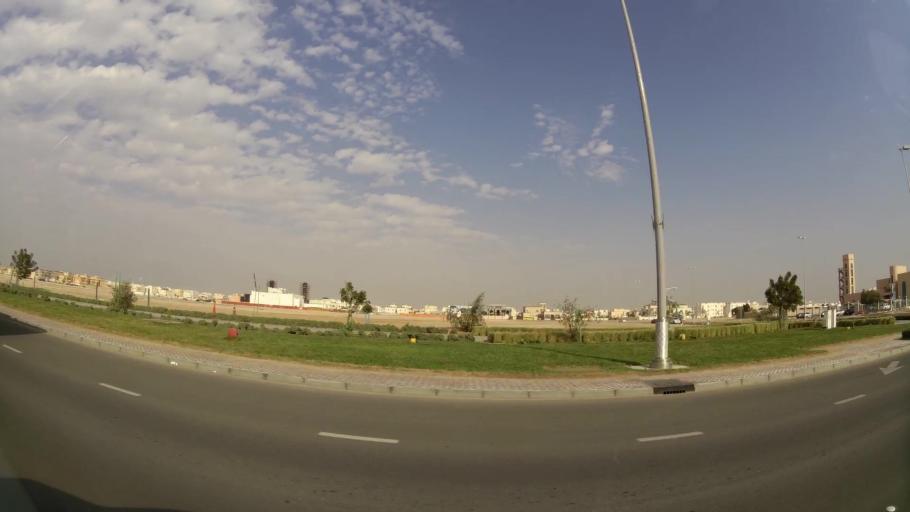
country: AE
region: Abu Dhabi
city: Abu Dhabi
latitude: 24.3616
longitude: 54.5373
